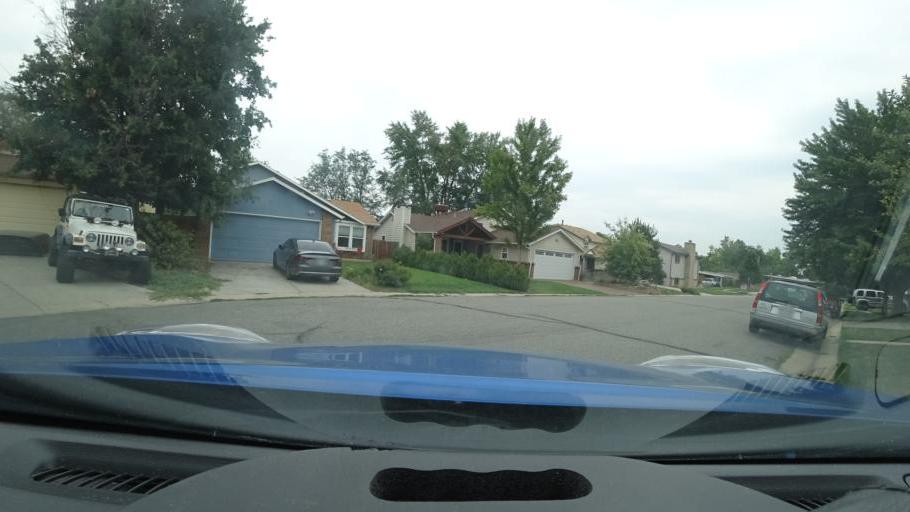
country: US
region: Colorado
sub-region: Arapahoe County
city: Glendale
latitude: 39.6889
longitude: -104.9172
